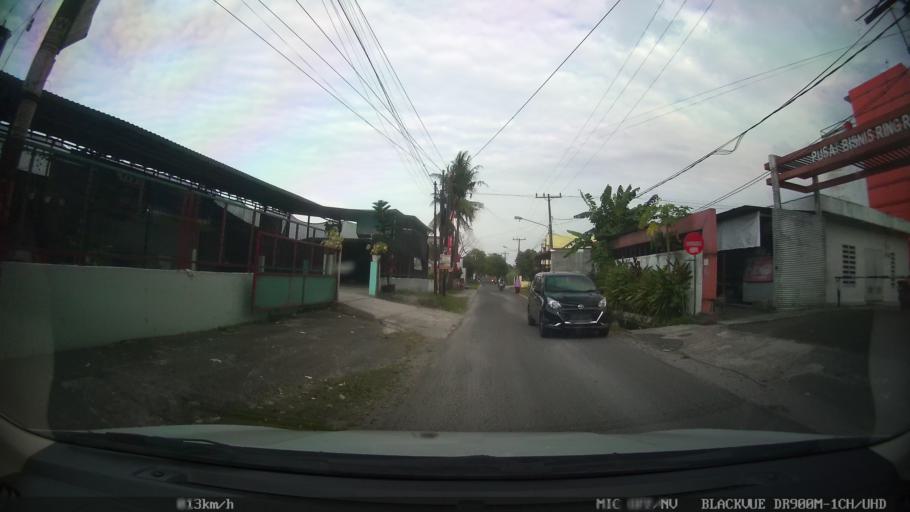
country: ID
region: North Sumatra
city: Sunggal
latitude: 3.5550
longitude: 98.6263
